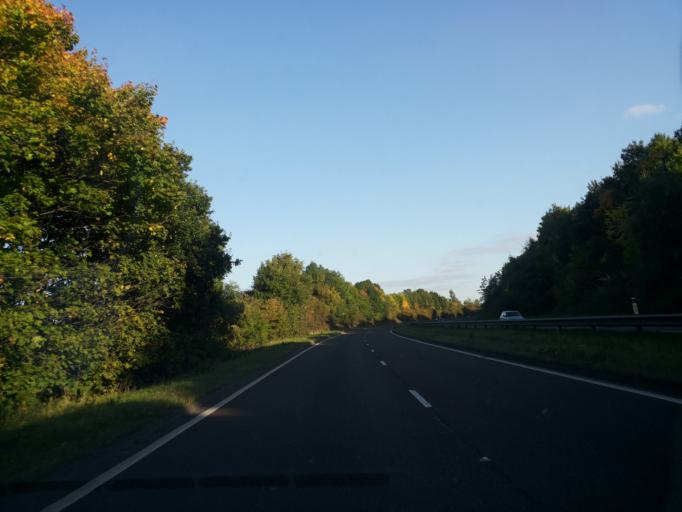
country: GB
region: England
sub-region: Derbyshire
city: Chesterfield
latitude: 53.2258
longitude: -1.4087
